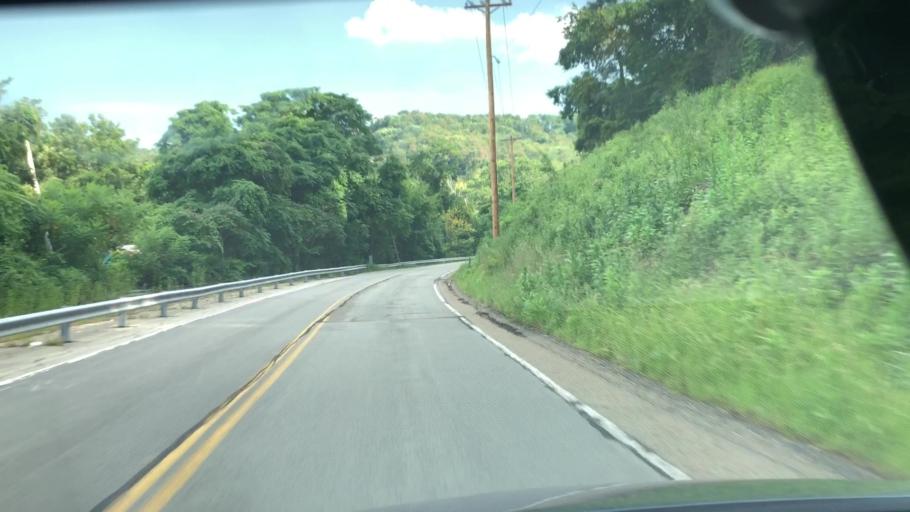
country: US
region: Pennsylvania
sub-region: Allegheny County
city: Blawnox
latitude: 40.4765
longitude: -79.8752
